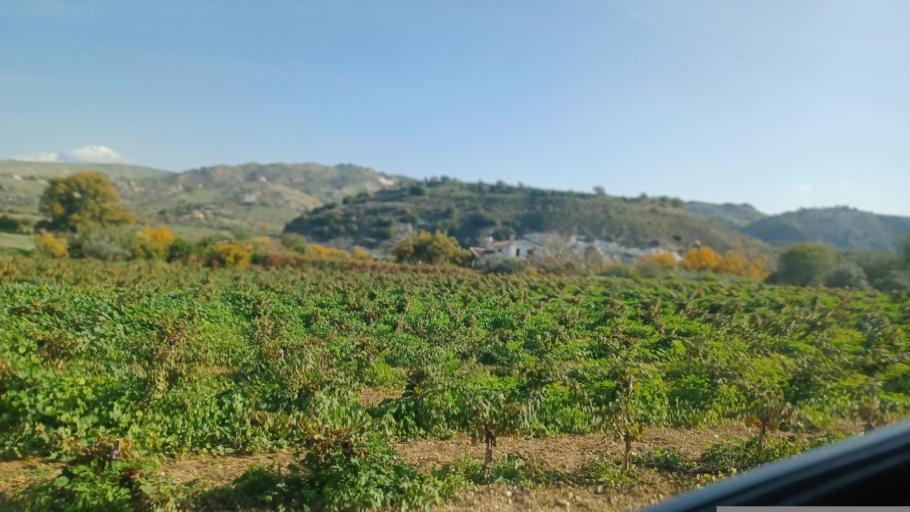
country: CY
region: Pafos
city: Mesogi
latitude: 34.7674
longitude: 32.5744
